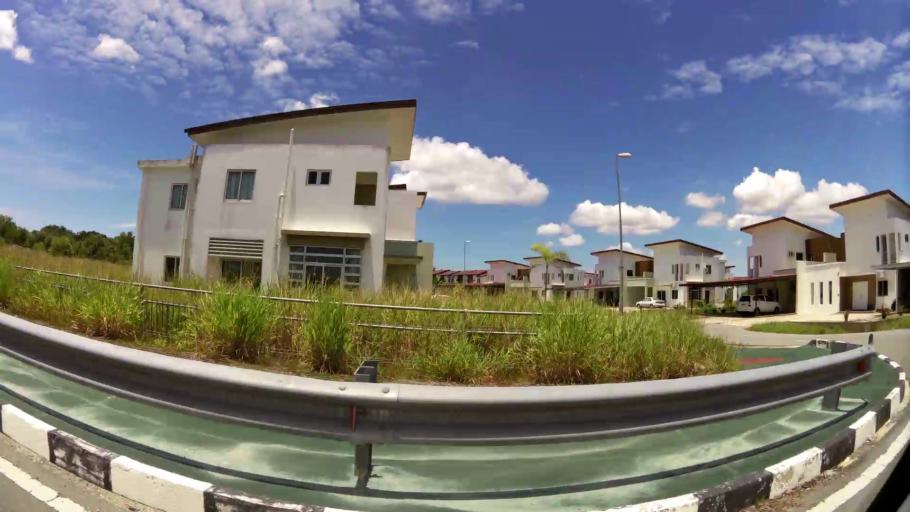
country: BN
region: Brunei and Muara
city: Bandar Seri Begawan
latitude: 5.0063
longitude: 115.0089
